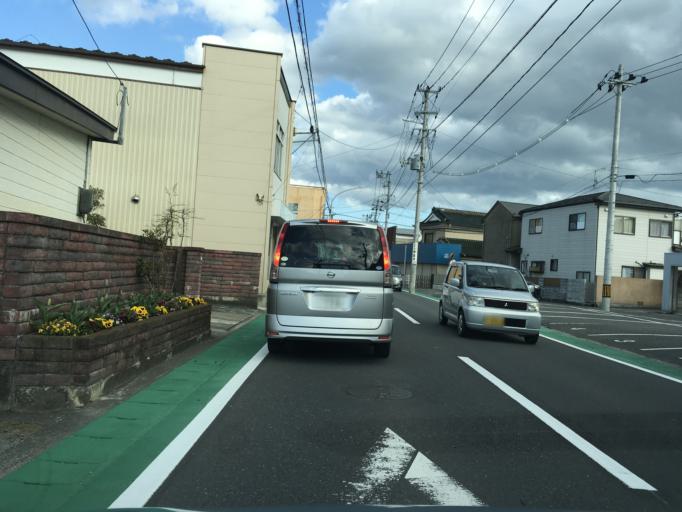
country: JP
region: Miyagi
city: Ishinomaki
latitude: 38.4378
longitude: 141.2944
